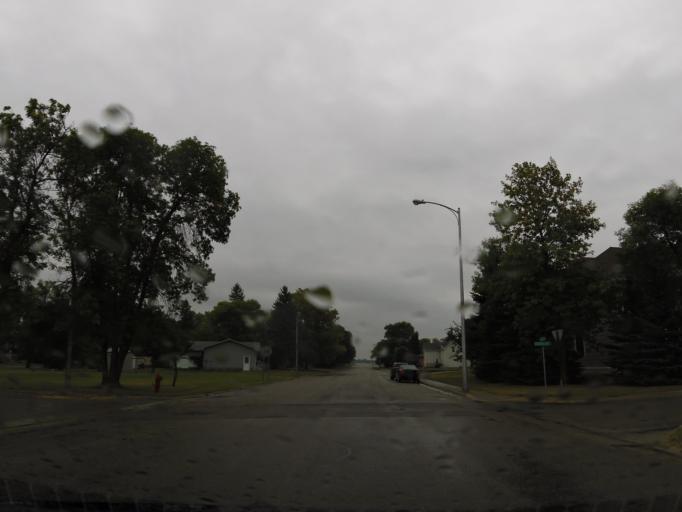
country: US
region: Minnesota
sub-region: Marshall County
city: Warren
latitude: 48.4490
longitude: -96.8728
